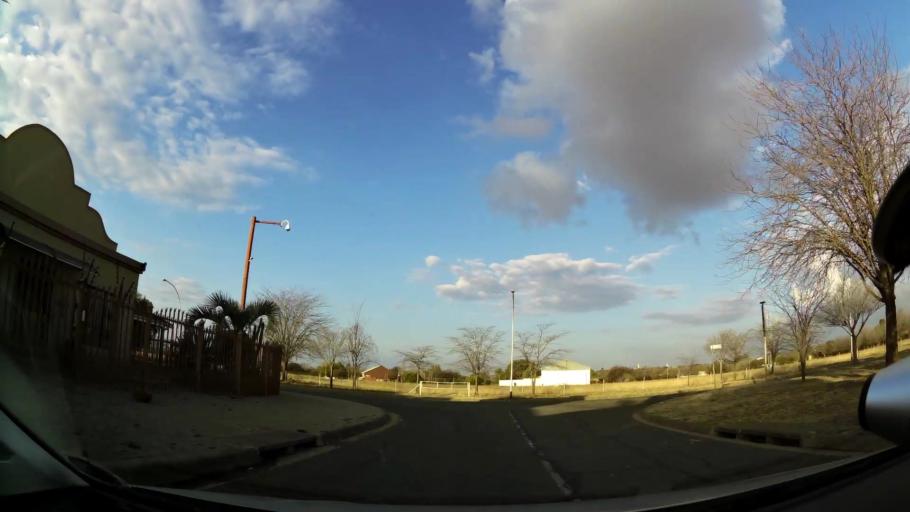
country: ZA
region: Orange Free State
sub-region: Mangaung Metropolitan Municipality
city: Bloemfontein
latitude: -29.1409
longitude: 26.1867
